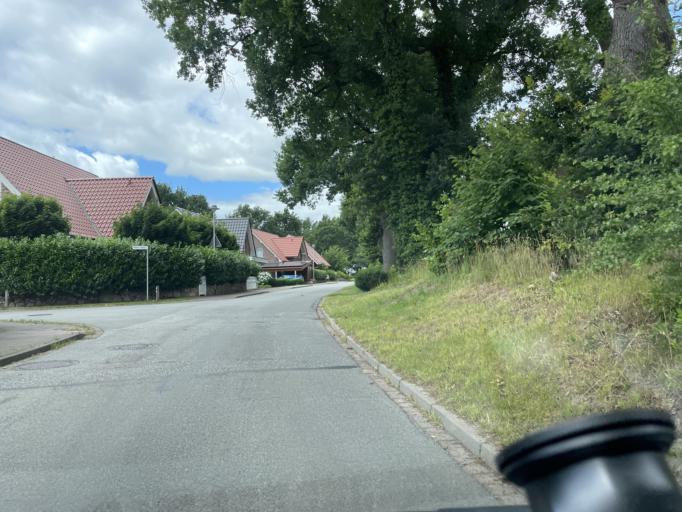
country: DE
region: Lower Saxony
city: Buxtehude
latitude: 53.4454
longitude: 9.7257
